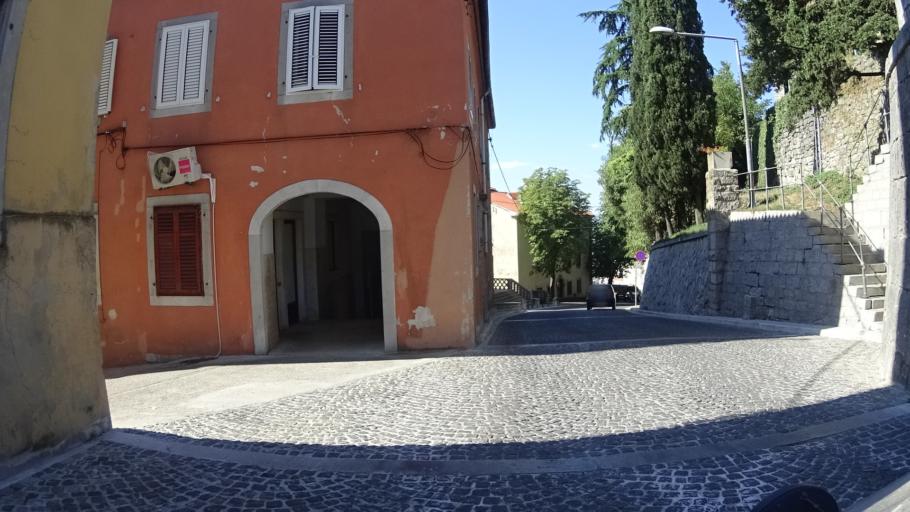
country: HR
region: Istarska
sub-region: Grad Labin
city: Labin
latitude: 45.0858
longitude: 14.1227
